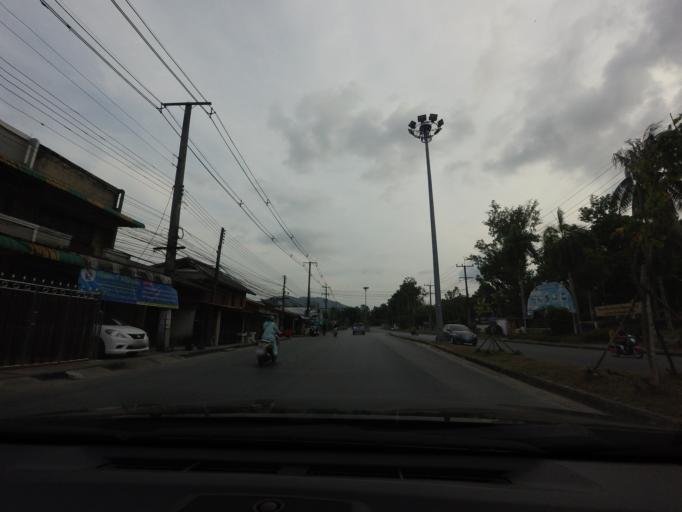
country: TH
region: Yala
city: Yala
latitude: 6.5249
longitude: 101.2825
